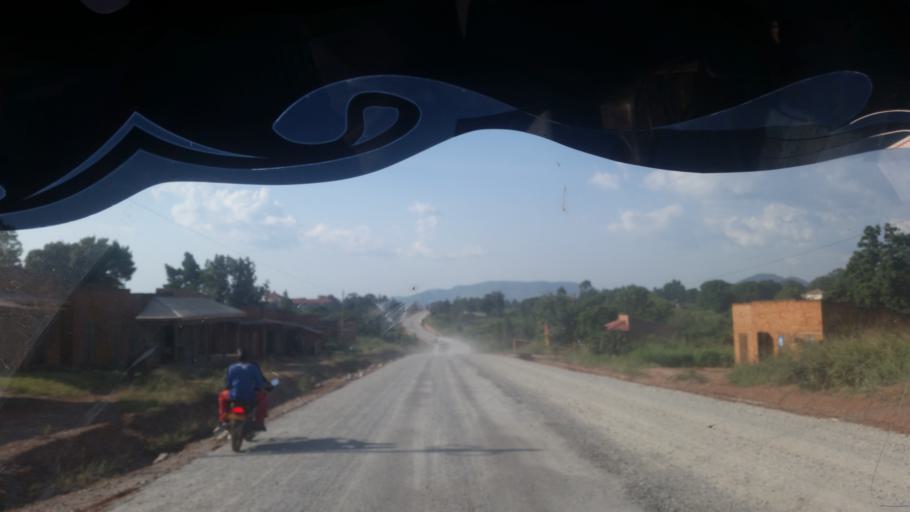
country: UG
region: Western Region
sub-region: Hoima District
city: Hoima
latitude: 1.3975
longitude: 31.3326
